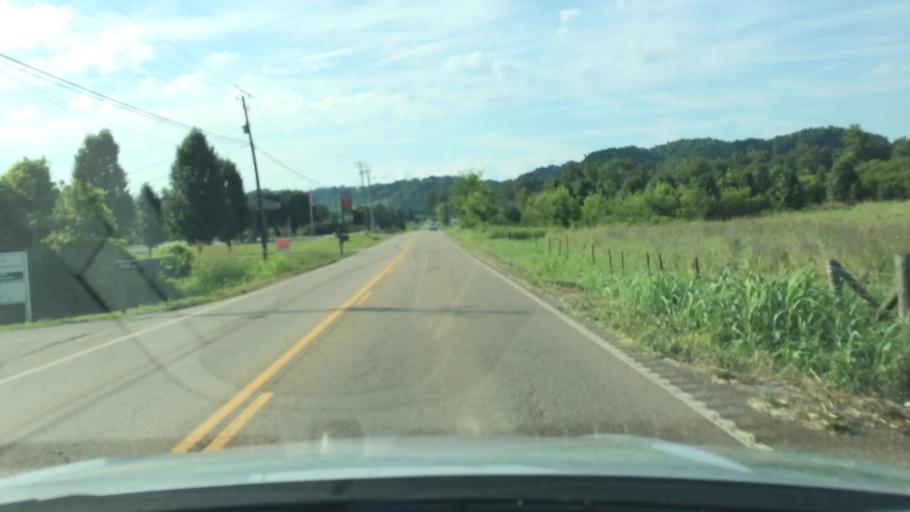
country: US
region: Tennessee
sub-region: Sevier County
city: Seymour
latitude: 35.9224
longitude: -83.6475
